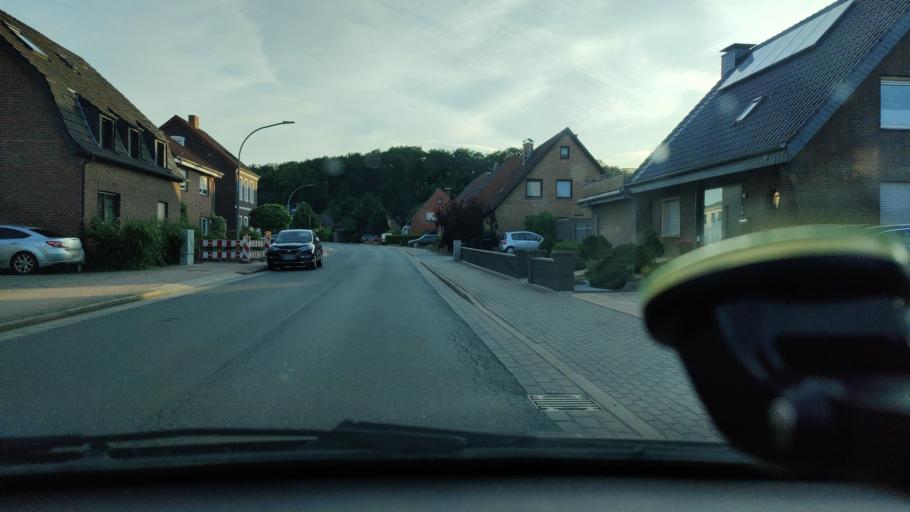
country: DE
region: North Rhine-Westphalia
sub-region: Regierungsbezirk Dusseldorf
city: Kamp-Lintfort
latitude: 51.4679
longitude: 6.5405
